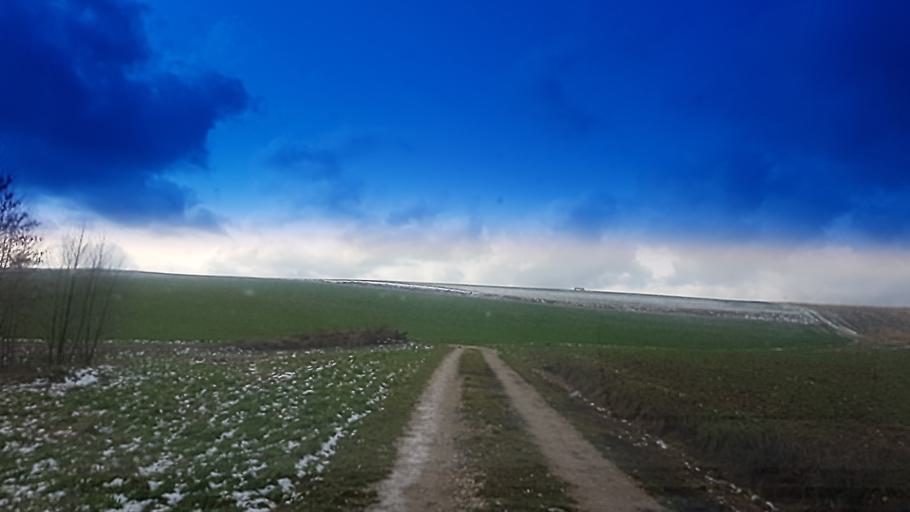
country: DE
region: Bavaria
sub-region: Upper Franconia
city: Schesslitz
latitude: 50.0055
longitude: 10.9993
